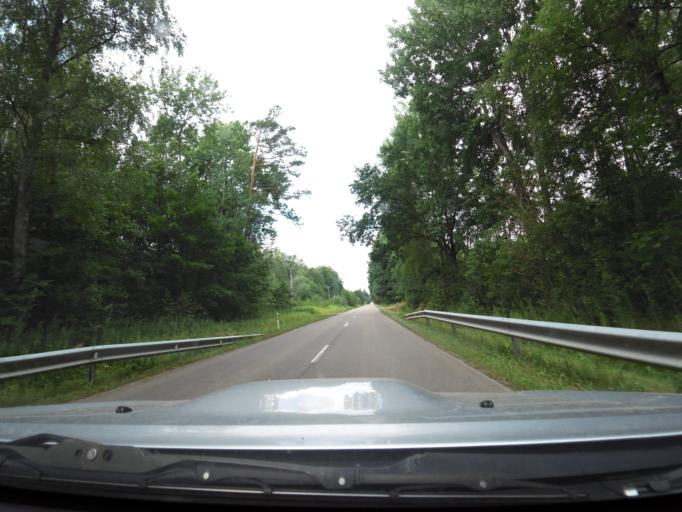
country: RU
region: Kaliningrad
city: Neman
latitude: 55.0919
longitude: 22.0283
